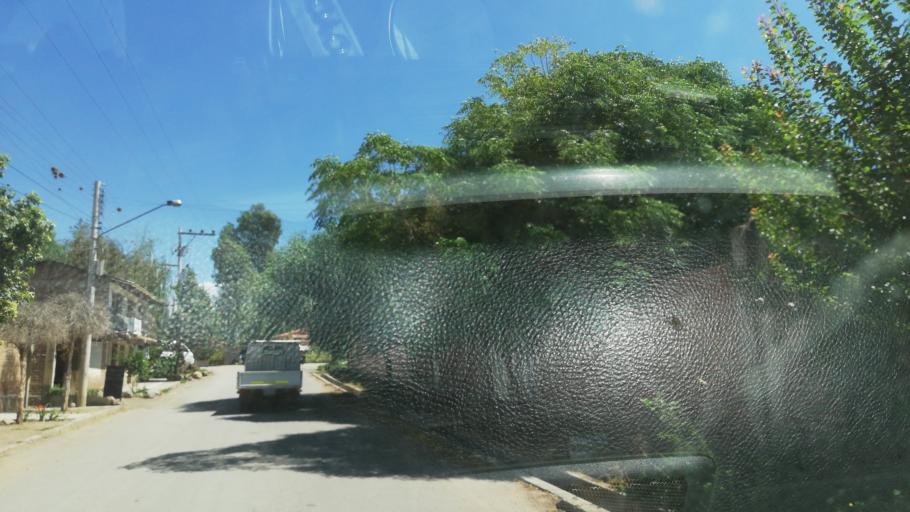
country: BO
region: Cochabamba
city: Cochabamba
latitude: -17.3760
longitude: -66.2068
